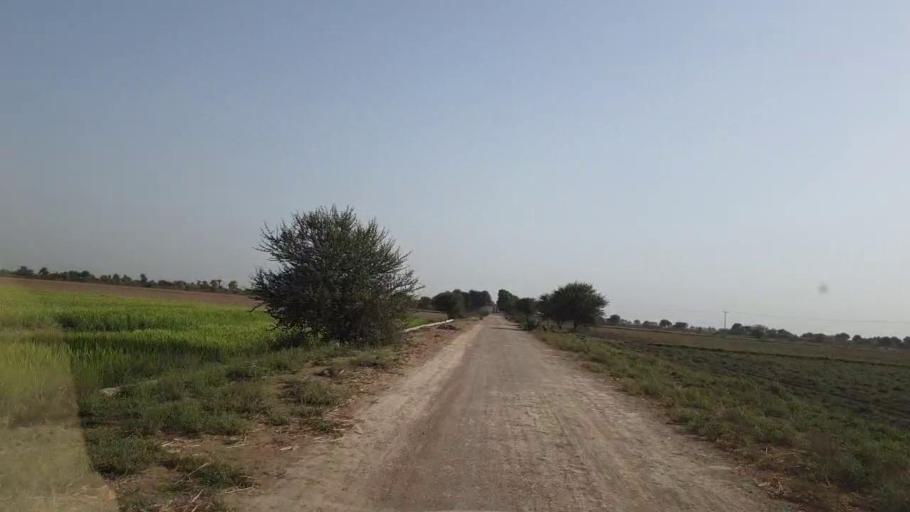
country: PK
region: Sindh
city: Tando Ghulam Ali
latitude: 25.0886
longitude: 68.8530
